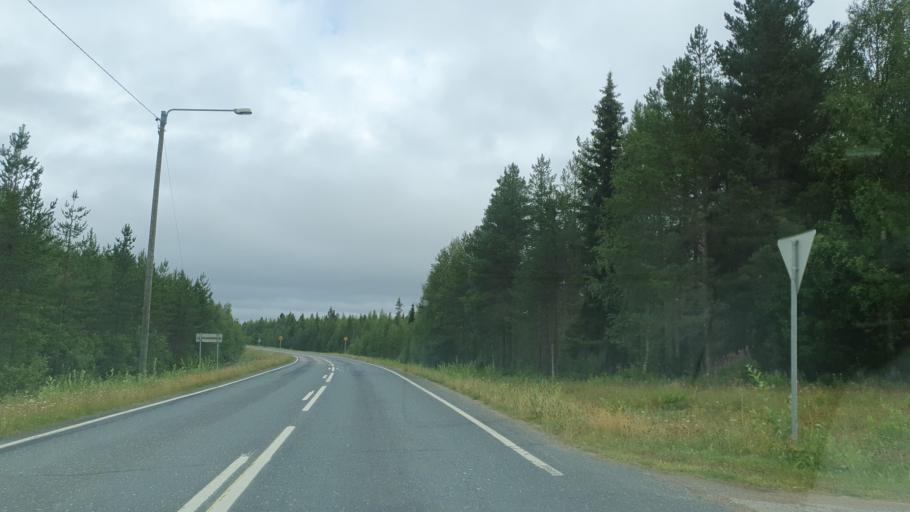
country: FI
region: Lapland
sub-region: Itae-Lappi
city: Pelkosenniemi
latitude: 67.1984
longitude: 27.4343
